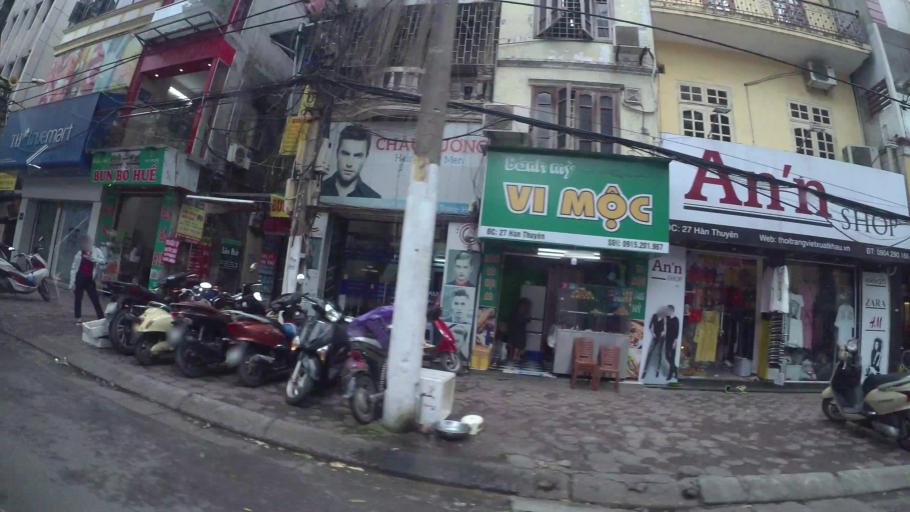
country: VN
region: Ha Noi
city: Hai BaTrung
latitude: 21.0184
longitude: 105.8557
